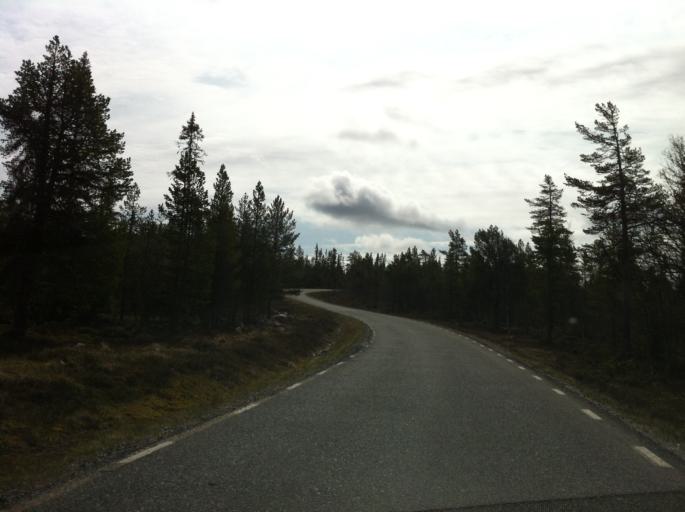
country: NO
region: Hedmark
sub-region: Engerdal
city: Engerdal
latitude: 62.3132
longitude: 12.8098
